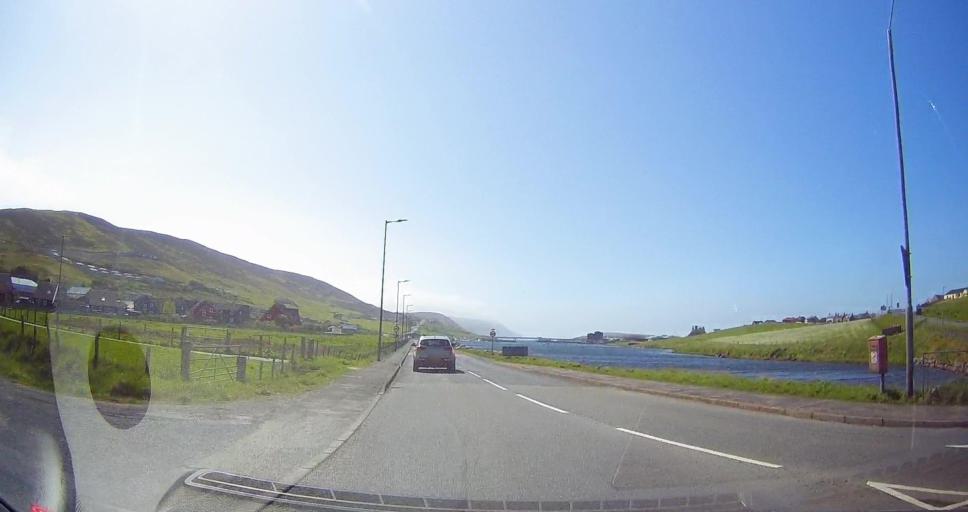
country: GB
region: Scotland
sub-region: Shetland Islands
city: Lerwick
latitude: 60.1422
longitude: -1.2659
